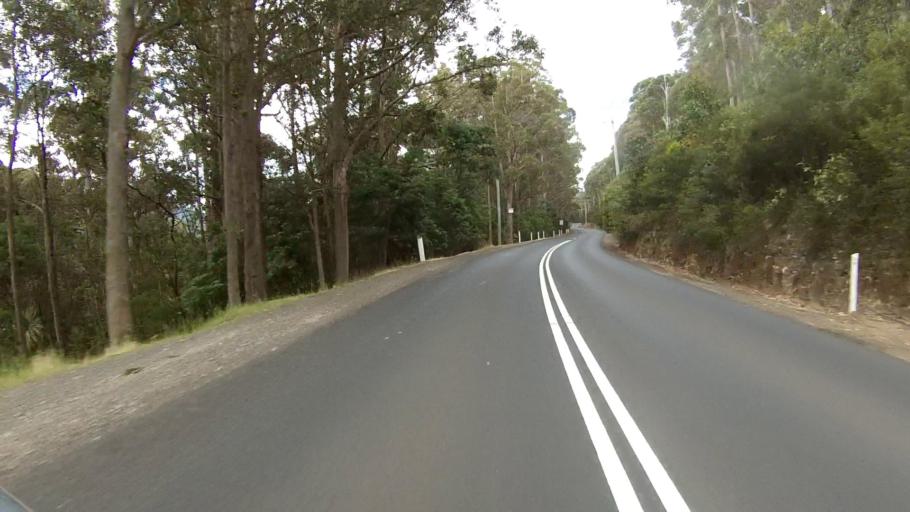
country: AU
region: Tasmania
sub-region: Hobart
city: Dynnyrne
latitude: -42.9121
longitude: 147.2694
